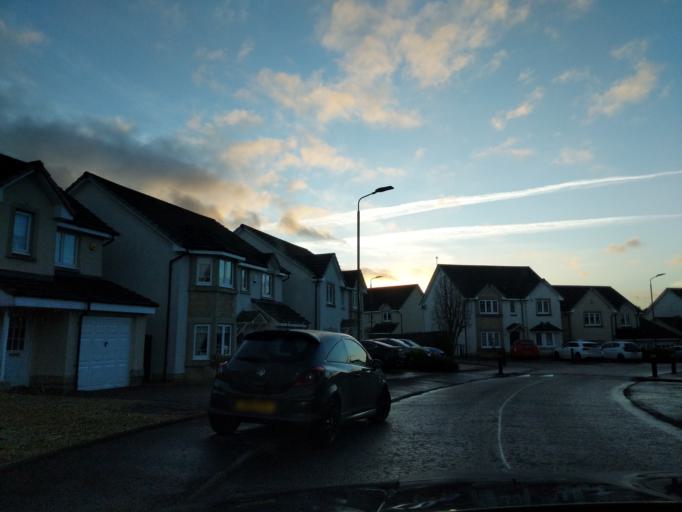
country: GB
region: Scotland
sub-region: Falkirk
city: Falkirk
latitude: 55.9854
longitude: -3.7932
